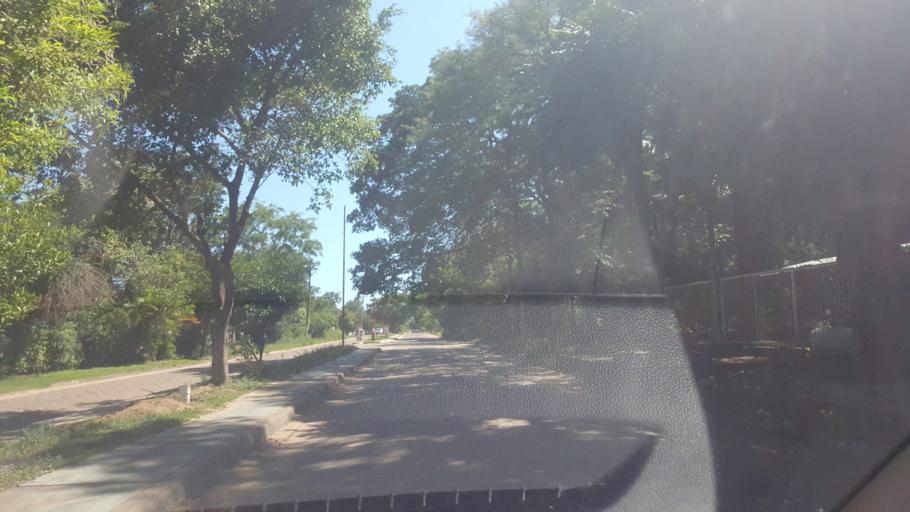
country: AR
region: Corrientes
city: Ituzaingo
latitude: -27.5922
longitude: -56.7015
